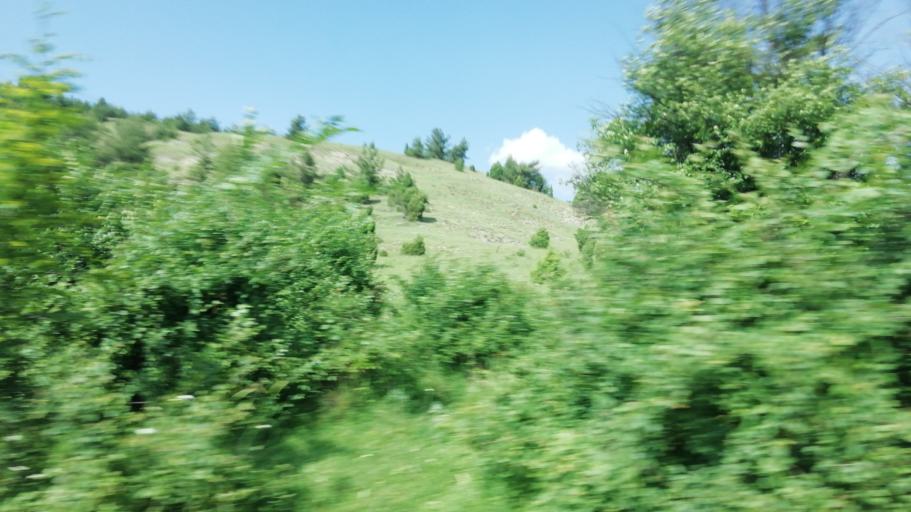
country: TR
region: Karabuk
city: Karabuk
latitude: 41.1312
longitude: 32.5670
